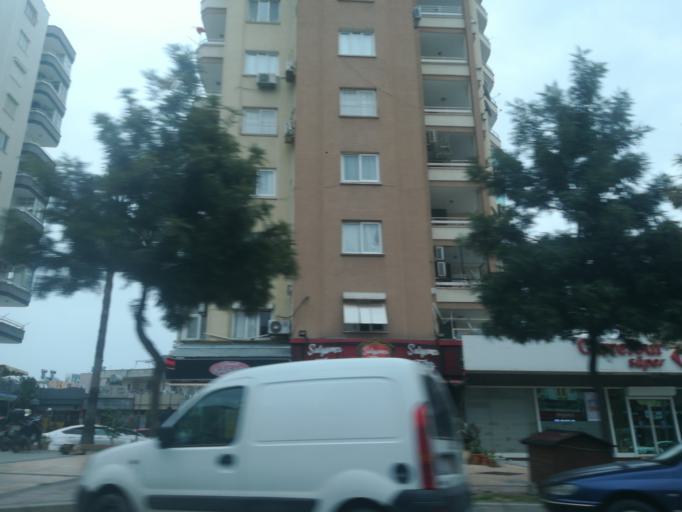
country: TR
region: Adana
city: Adana
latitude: 37.0331
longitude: 35.3088
